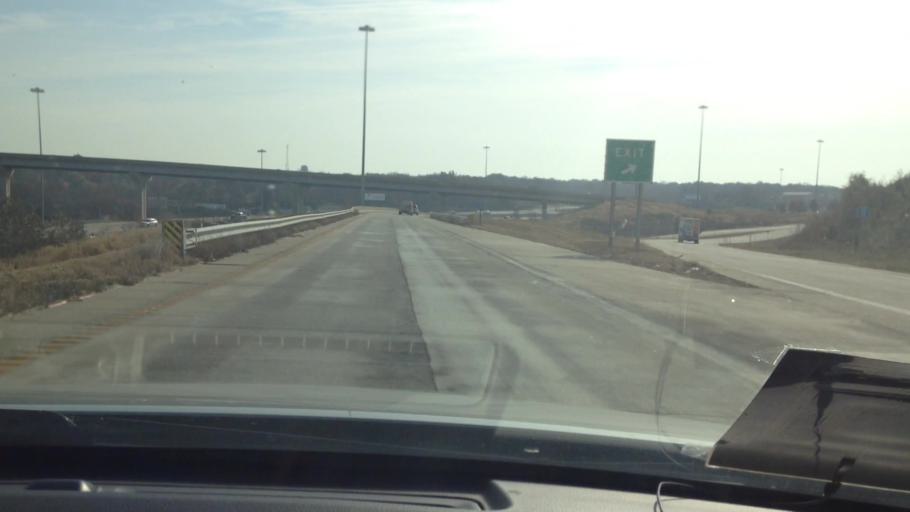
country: US
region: Missouri
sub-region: Jackson County
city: Grandview
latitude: 38.9330
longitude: -94.5307
